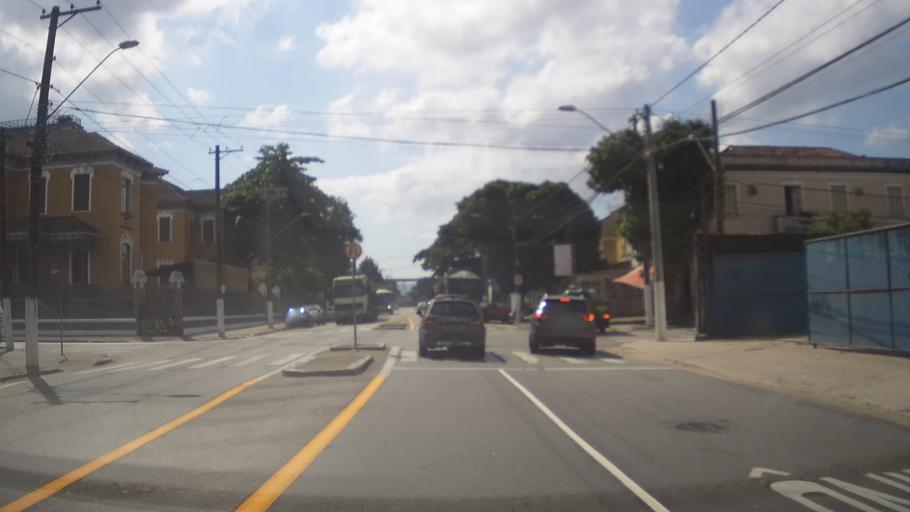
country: BR
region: Sao Paulo
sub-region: Santos
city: Santos
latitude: -23.9566
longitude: -46.3124
